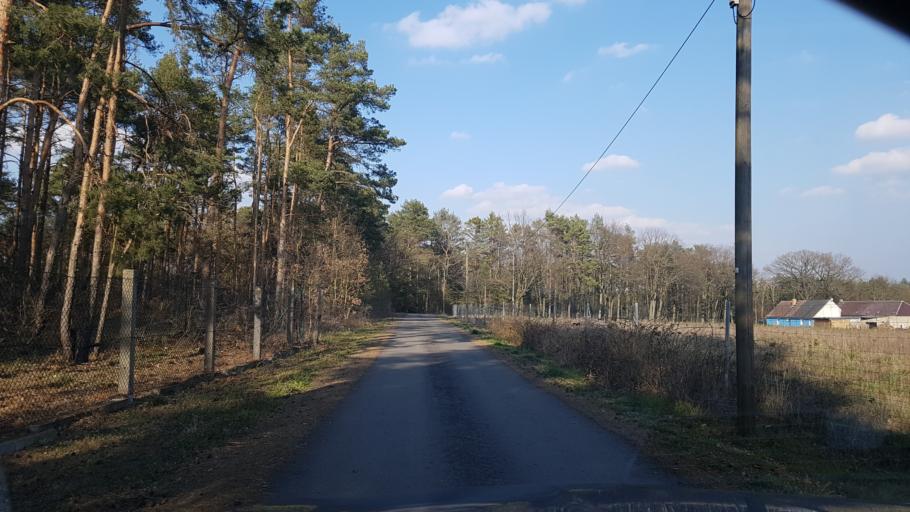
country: DE
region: Brandenburg
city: Bad Liebenwerda
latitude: 51.5229
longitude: 13.4183
